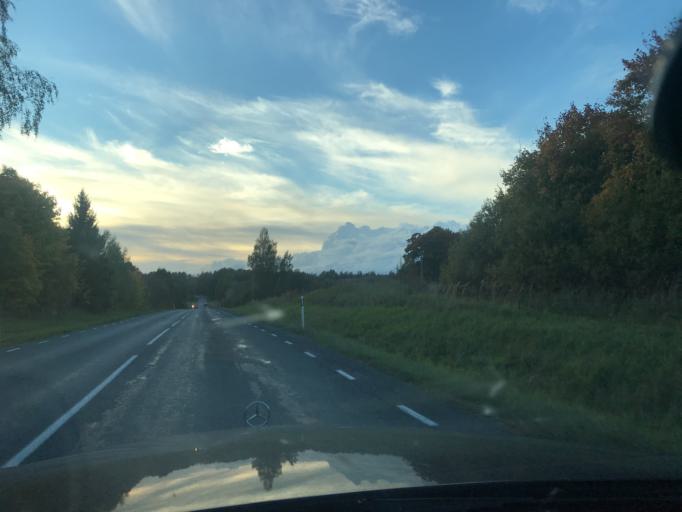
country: EE
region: Vorumaa
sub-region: Antsla vald
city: Vana-Antsla
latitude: 57.8774
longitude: 26.6539
